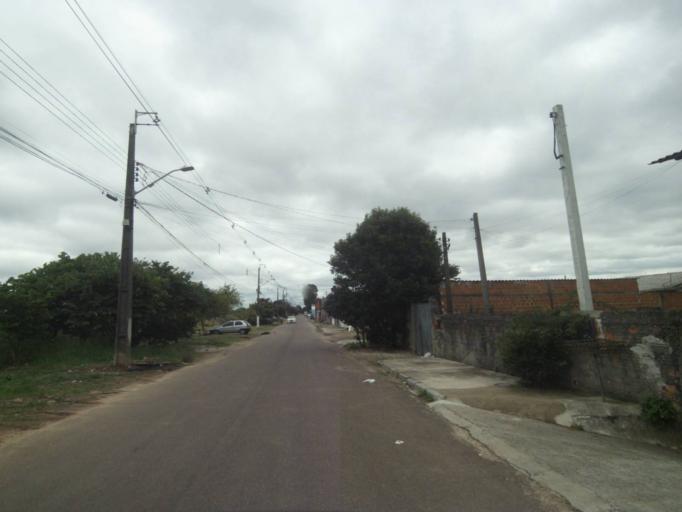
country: BR
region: Parana
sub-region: Pinhais
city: Pinhais
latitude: -25.4582
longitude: -49.1994
